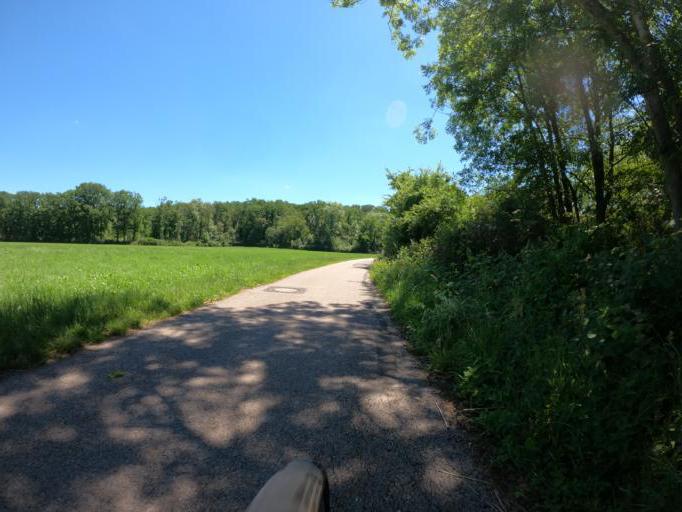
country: DE
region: Baden-Wuerttemberg
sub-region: Regierungsbezirk Stuttgart
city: Vaihingen an der Enz
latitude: 48.9623
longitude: 8.9686
